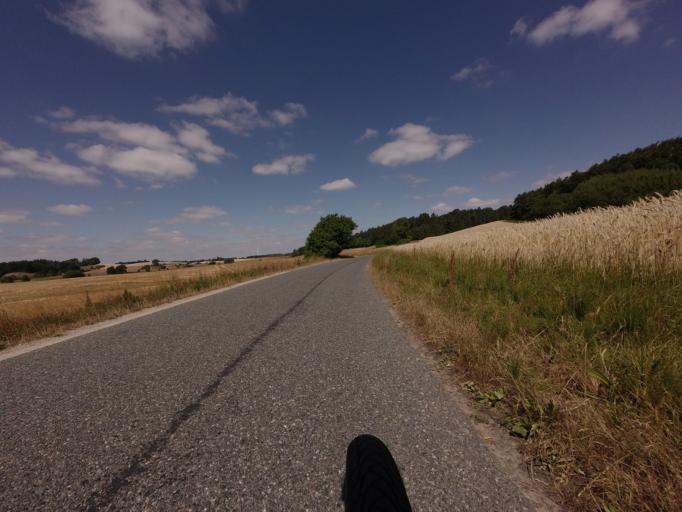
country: DK
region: Central Jutland
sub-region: Odder Kommune
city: Odder
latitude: 55.9000
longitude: 10.0646
